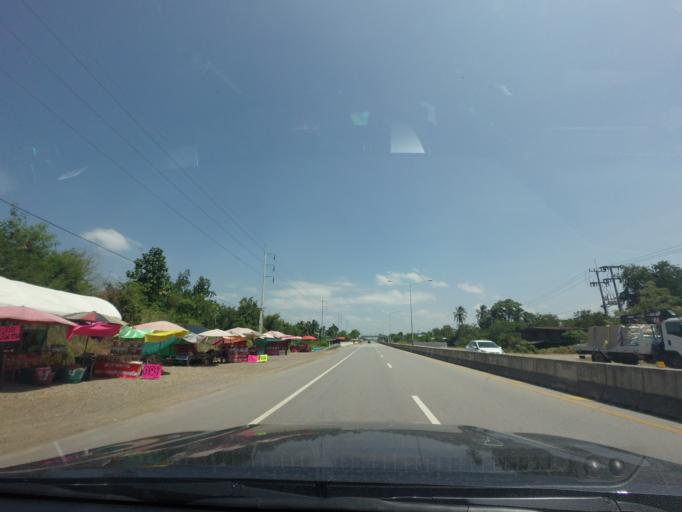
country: TH
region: Phetchabun
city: Lom Sak
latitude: 16.7635
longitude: 101.1484
